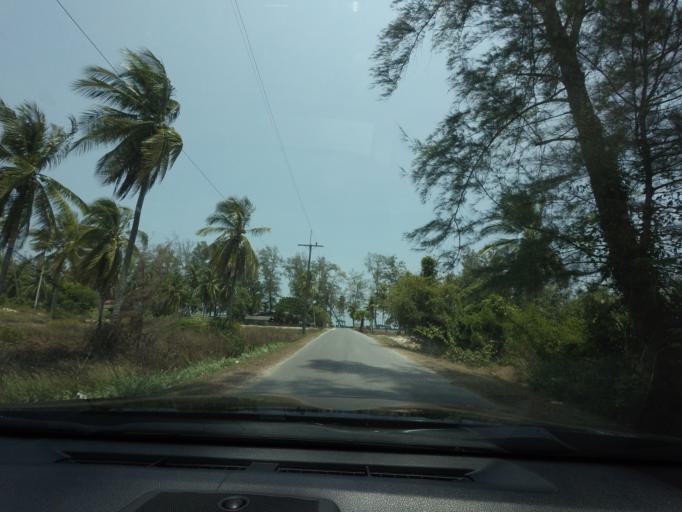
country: TH
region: Pattani
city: Yaring
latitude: 6.8977
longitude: 101.3710
